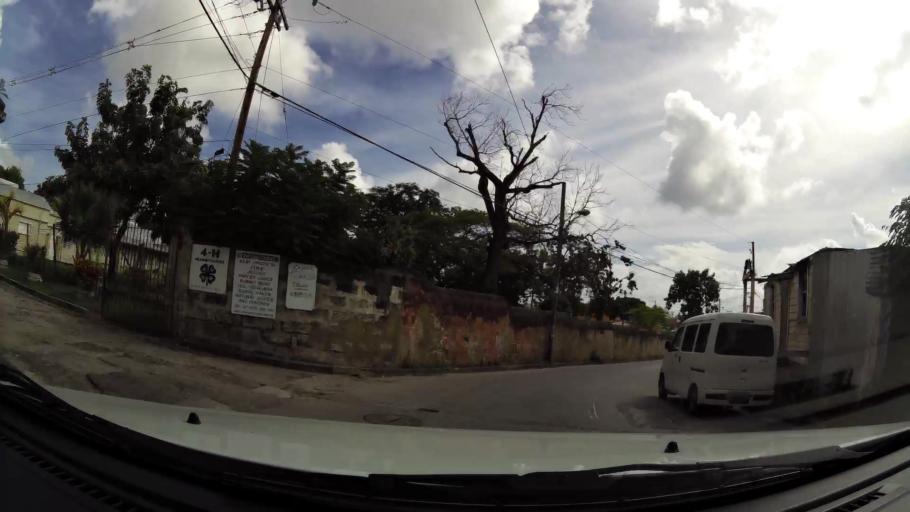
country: BB
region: Saint Michael
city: Bridgetown
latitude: 13.0987
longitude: -59.6110
